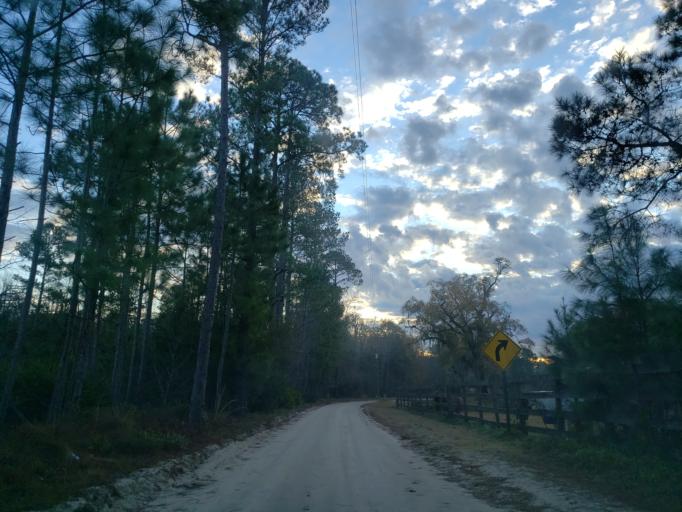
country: US
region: Georgia
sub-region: Chatham County
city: Bloomingdale
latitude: 32.1141
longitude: -81.3465
